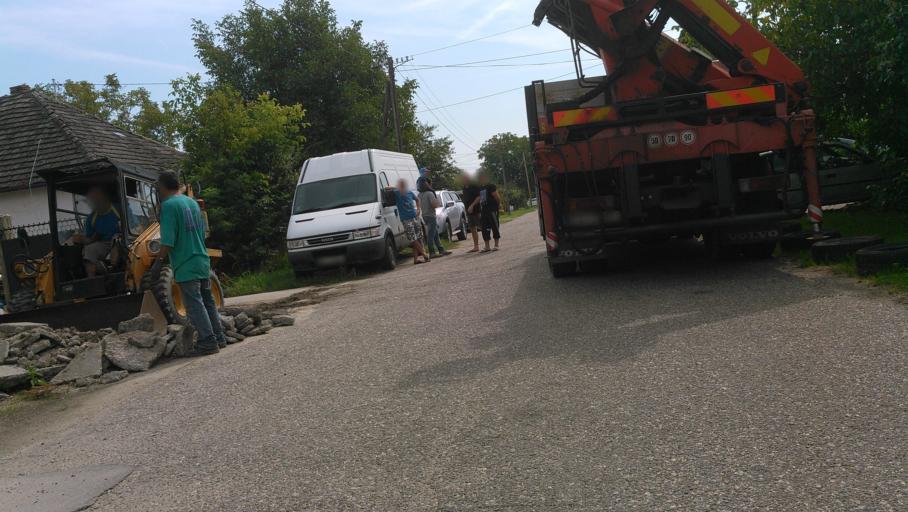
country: SK
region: Nitriansky
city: Kolarovo
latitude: 47.9090
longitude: 17.9932
